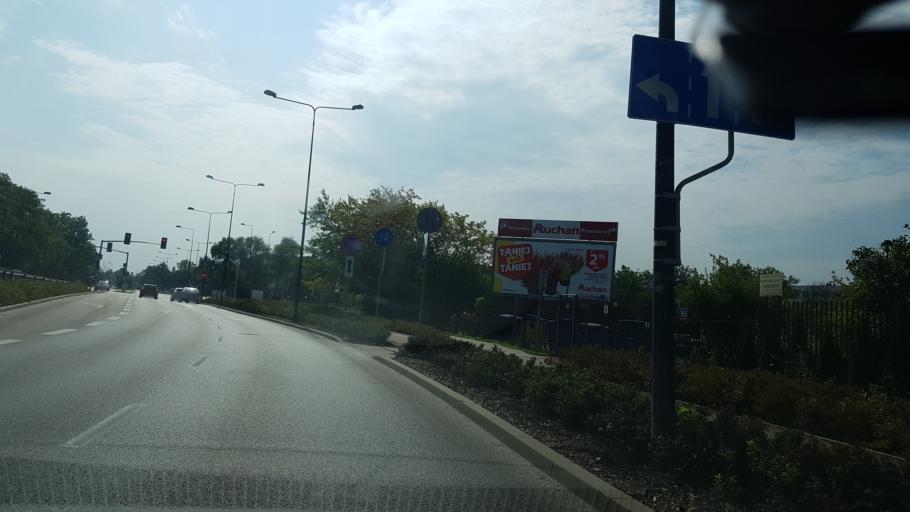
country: PL
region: Masovian Voivodeship
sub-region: Warszawa
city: Ursynow
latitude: 52.1658
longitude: 21.0448
